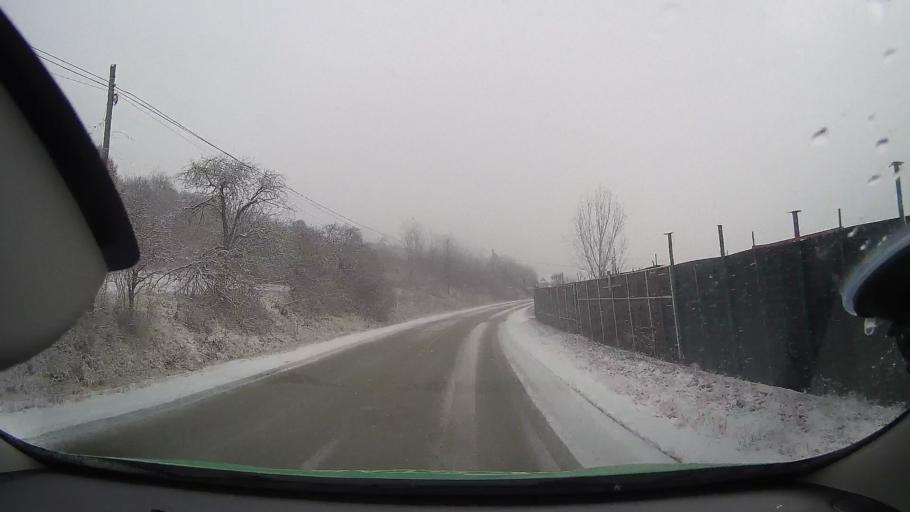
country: RO
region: Alba
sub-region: Comuna Livezile
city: Livezile
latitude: 46.3463
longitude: 23.6515
